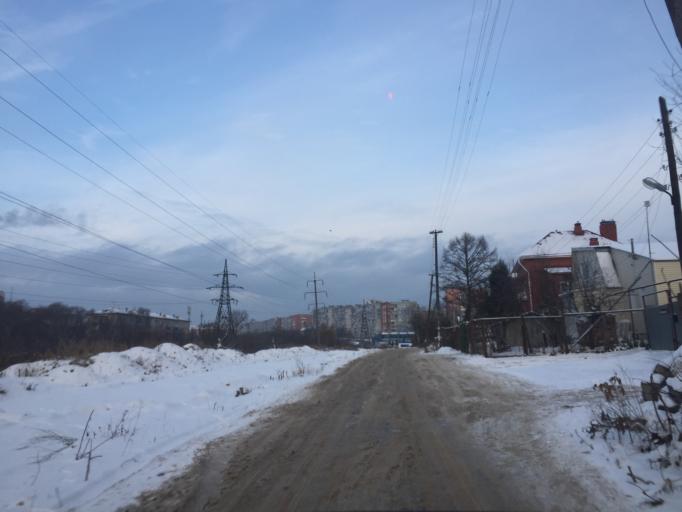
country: RU
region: Tula
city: Tula
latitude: 54.2015
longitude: 37.6747
